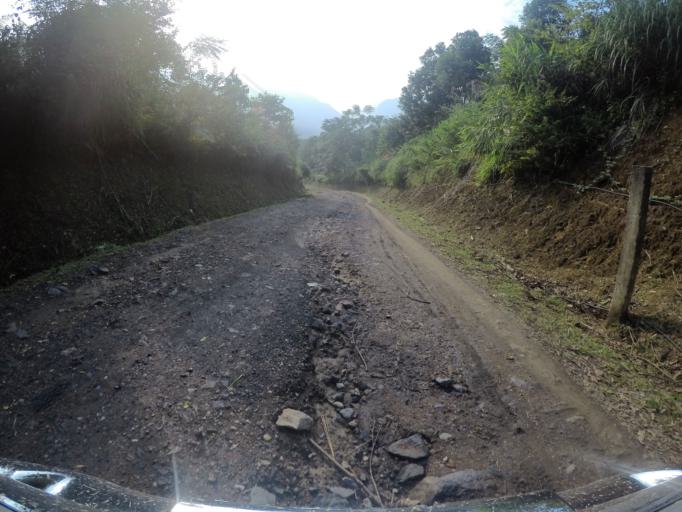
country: VN
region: Yen Bai
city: Son Thinh
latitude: 21.6825
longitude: 104.6212
